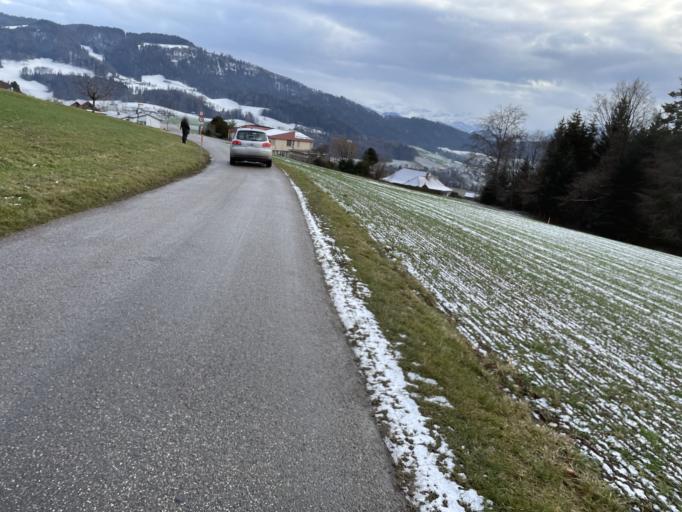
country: CH
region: Lucerne
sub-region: Entlebuch District
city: Oberdiessbach
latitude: 46.8404
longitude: 7.6052
